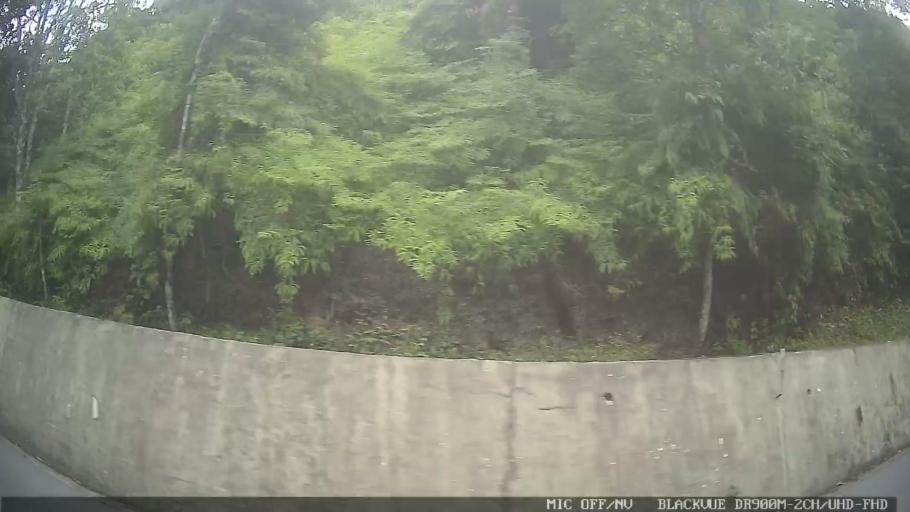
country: BR
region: Sao Paulo
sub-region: Caraguatatuba
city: Caraguatatuba
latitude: -23.5989
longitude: -45.4479
